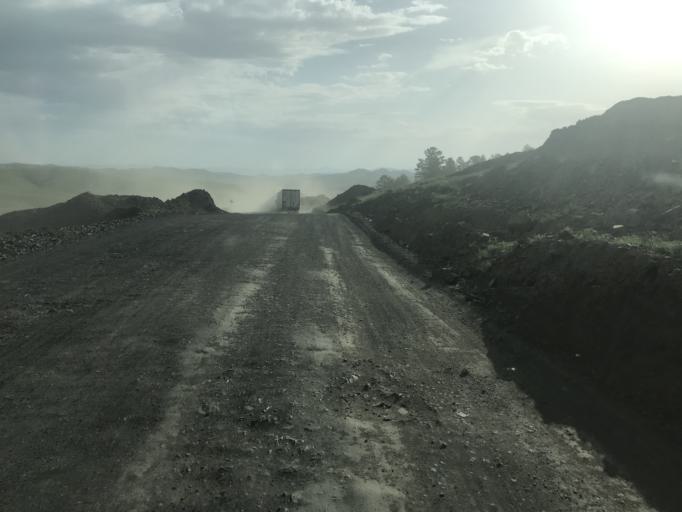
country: MN
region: Central Aimak
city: Javhlant
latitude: 48.6470
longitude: 106.0927
